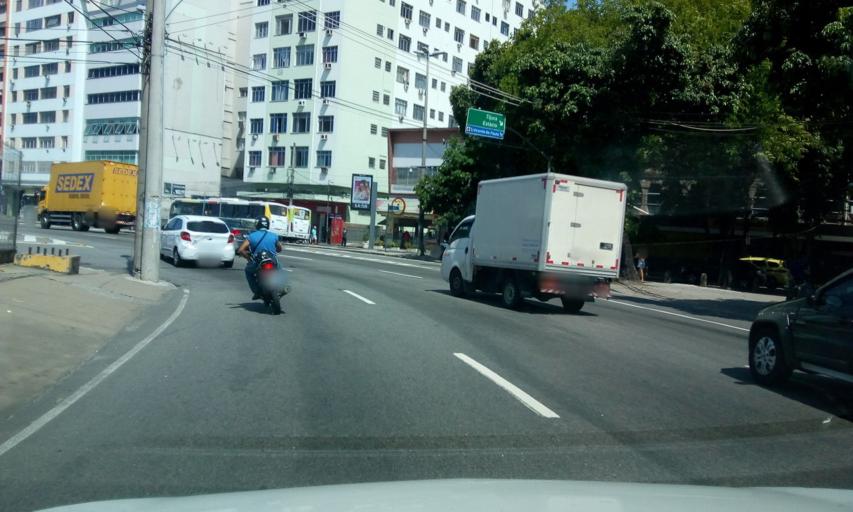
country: BR
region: Rio de Janeiro
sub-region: Rio De Janeiro
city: Rio de Janeiro
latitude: -22.9117
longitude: -43.2153
